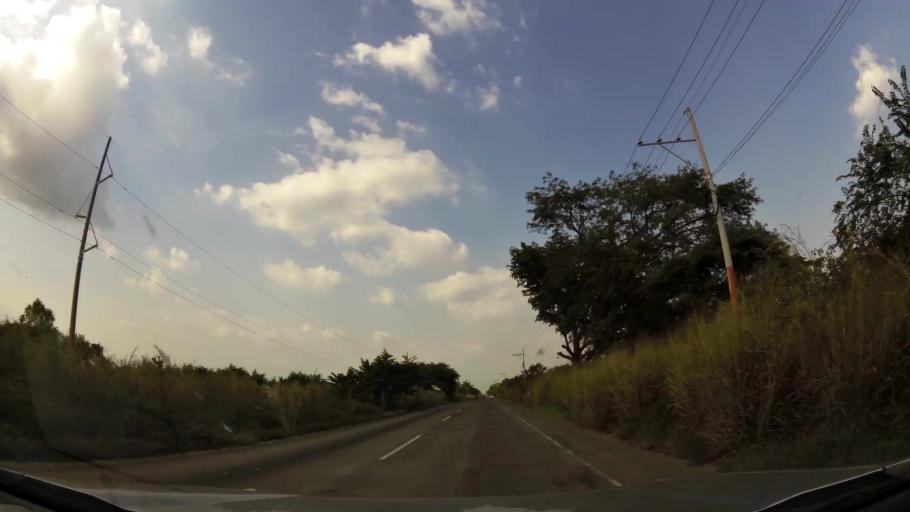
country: GT
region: Escuintla
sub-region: Municipio de Masagua
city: Masagua
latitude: 14.1081
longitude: -90.7806
